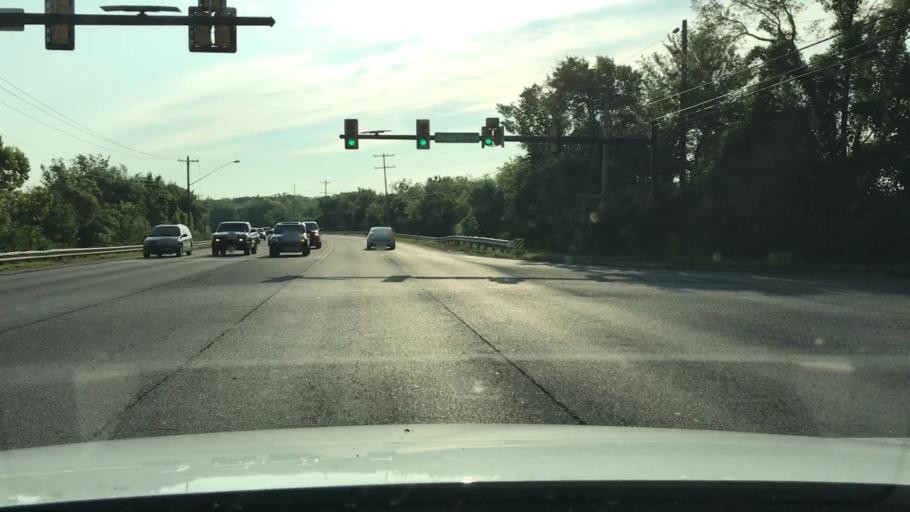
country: US
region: Tennessee
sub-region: Sumner County
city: Gallatin
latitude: 36.3489
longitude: -86.5150
